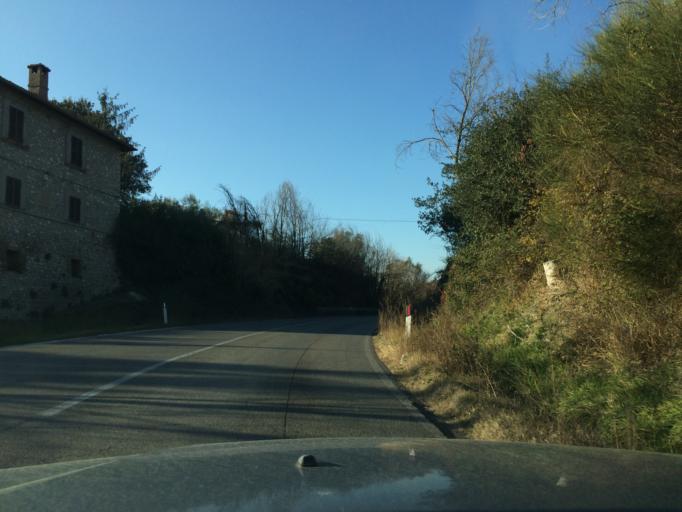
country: IT
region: Umbria
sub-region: Provincia di Terni
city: Fornole
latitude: 42.5394
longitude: 12.4691
